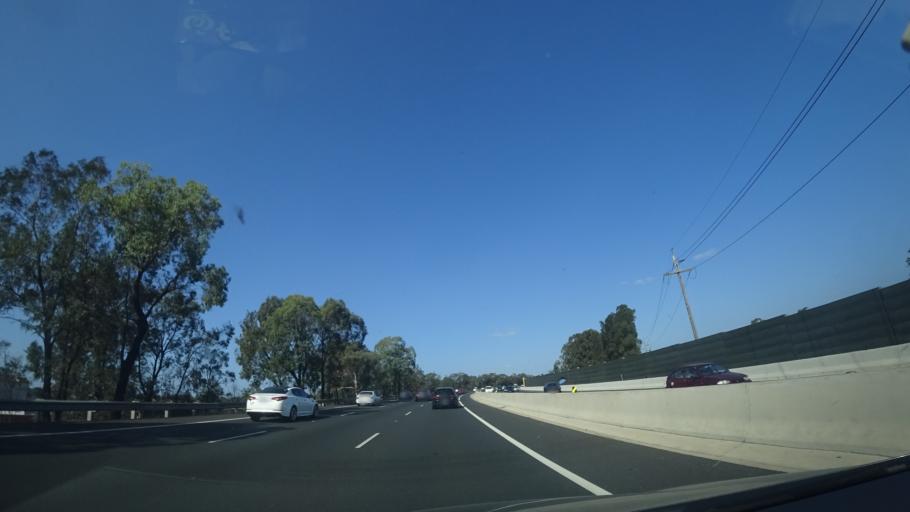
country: AU
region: New South Wales
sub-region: Bankstown
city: Revesby
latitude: -33.9399
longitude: 151.0063
